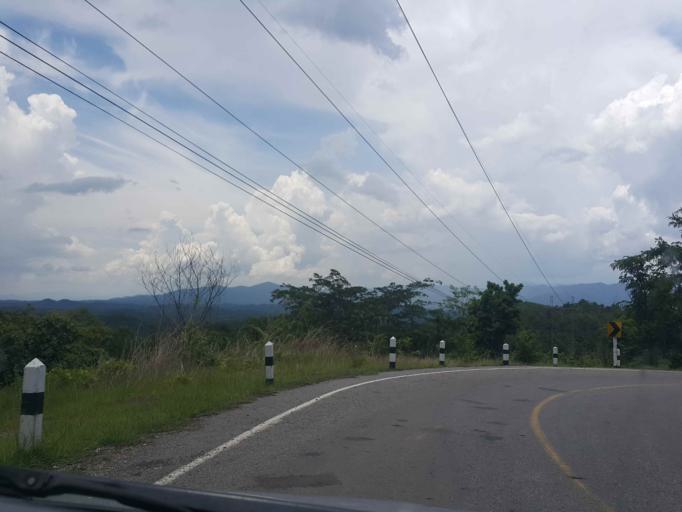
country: TH
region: Phayao
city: Chiang Muan
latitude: 18.9223
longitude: 100.2029
